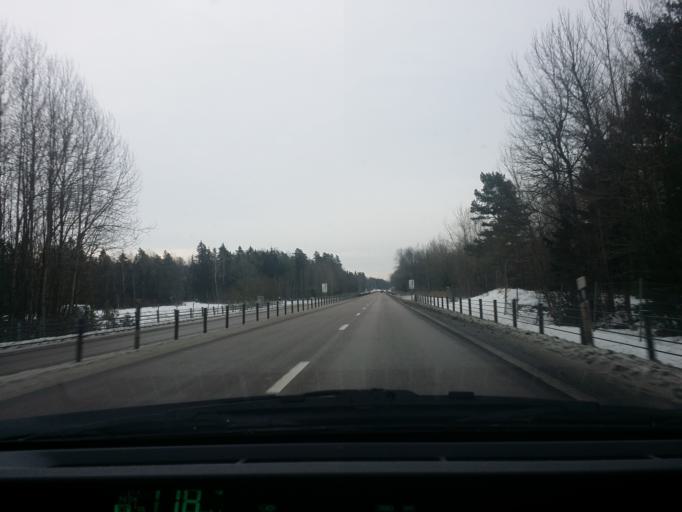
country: SE
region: Vaestra Goetaland
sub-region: Skovde Kommun
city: Stopen
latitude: 58.5209
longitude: 13.8273
